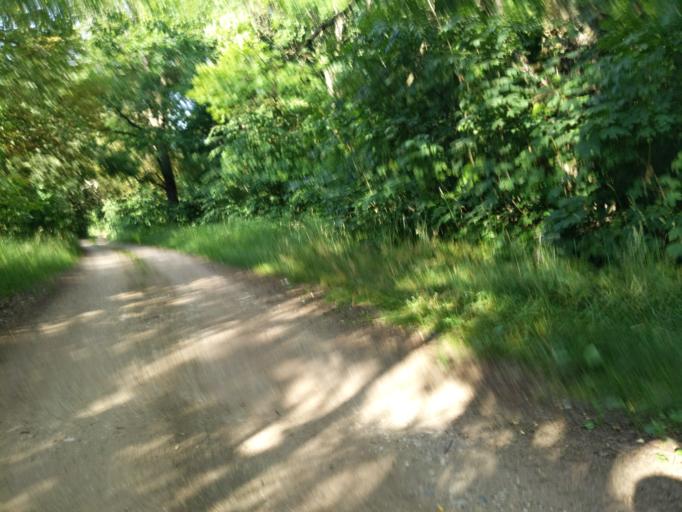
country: BY
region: Minsk
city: Nyasvizh
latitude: 53.2336
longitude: 26.7031
